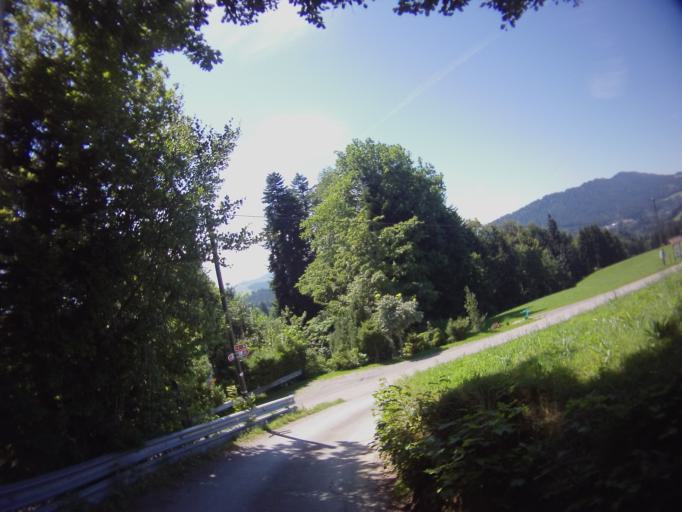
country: CH
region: Schwyz
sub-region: Bezirk Hoefe
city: Feusisberg
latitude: 47.1734
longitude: 8.7465
